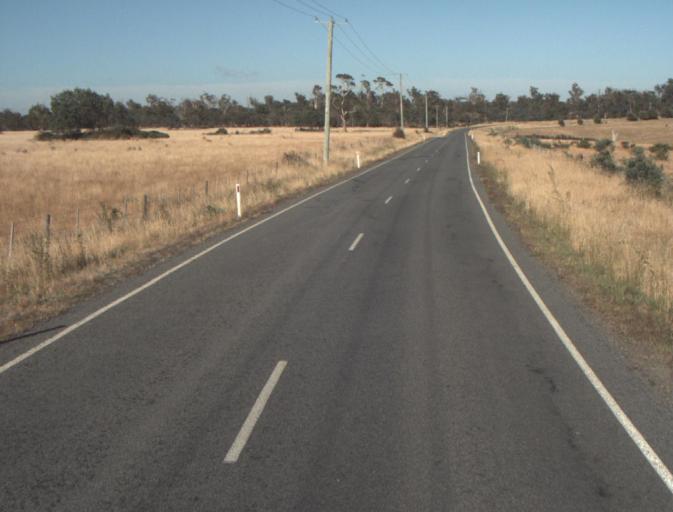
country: AU
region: Tasmania
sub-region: Launceston
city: Newstead
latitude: -41.4458
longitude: 147.2508
